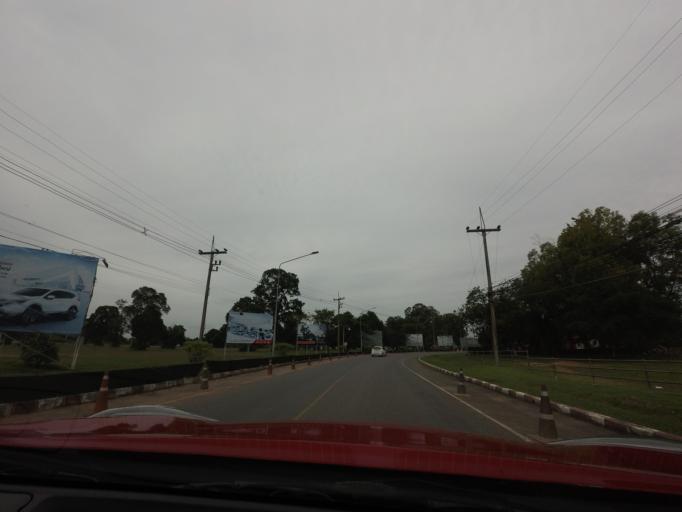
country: TH
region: Songkhla
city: Khlong Hoi Khong
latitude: 6.9383
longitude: 100.3958
